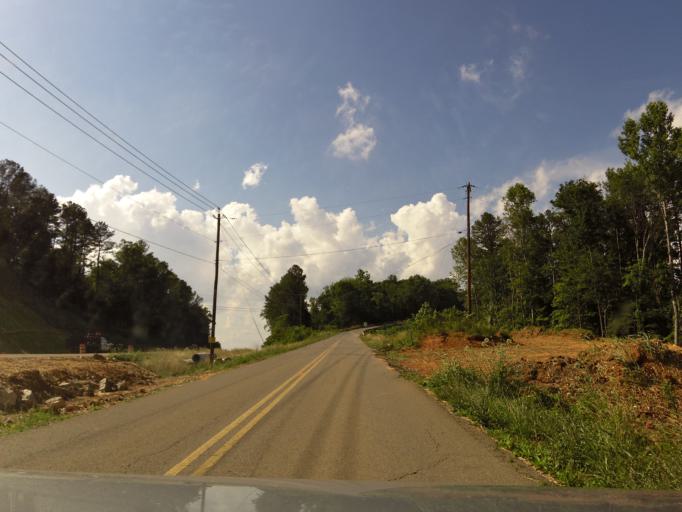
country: US
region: Tennessee
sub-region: Union County
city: Condon
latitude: 36.1367
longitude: -83.9132
